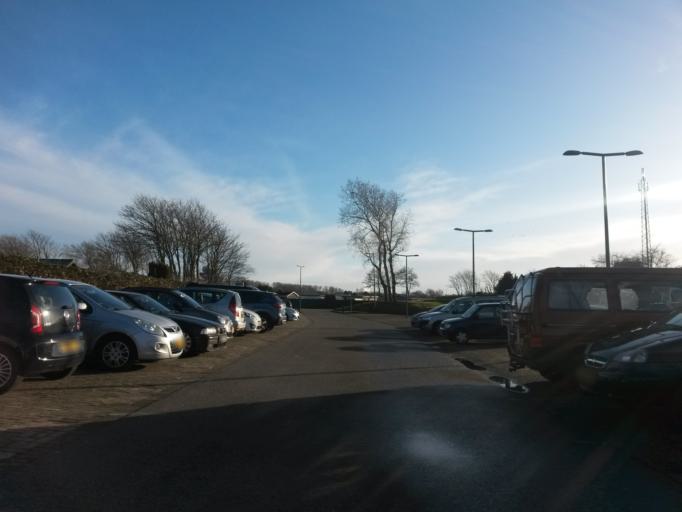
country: NL
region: South Holland
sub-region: Gemeente Rotterdam
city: Hoek van Holland
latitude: 51.9930
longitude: 4.1266
